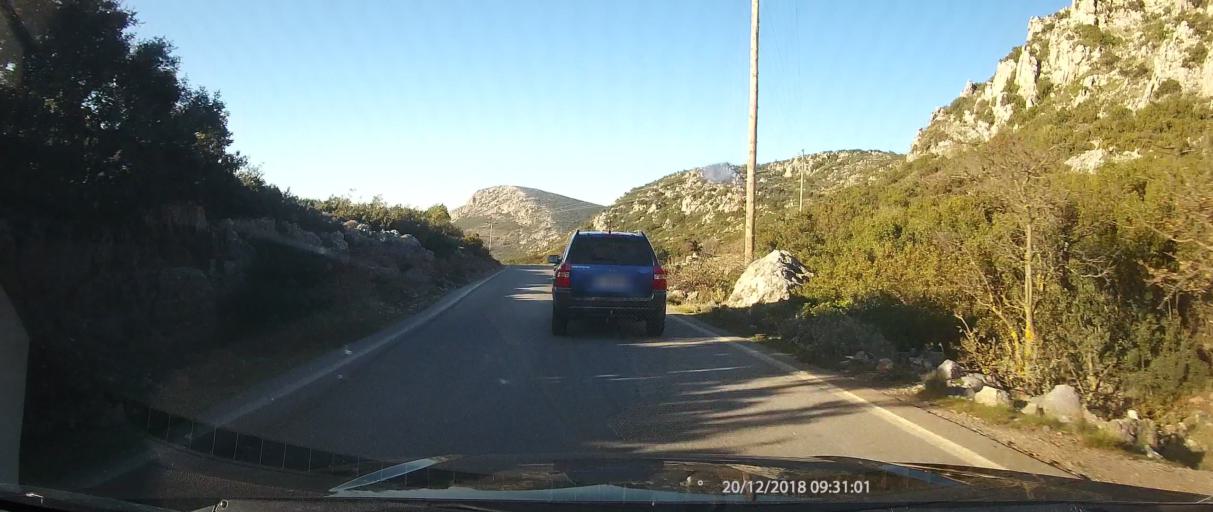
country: GR
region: Peloponnese
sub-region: Nomos Lakonias
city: Kato Glikovrisi
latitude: 36.9524
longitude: 22.8396
